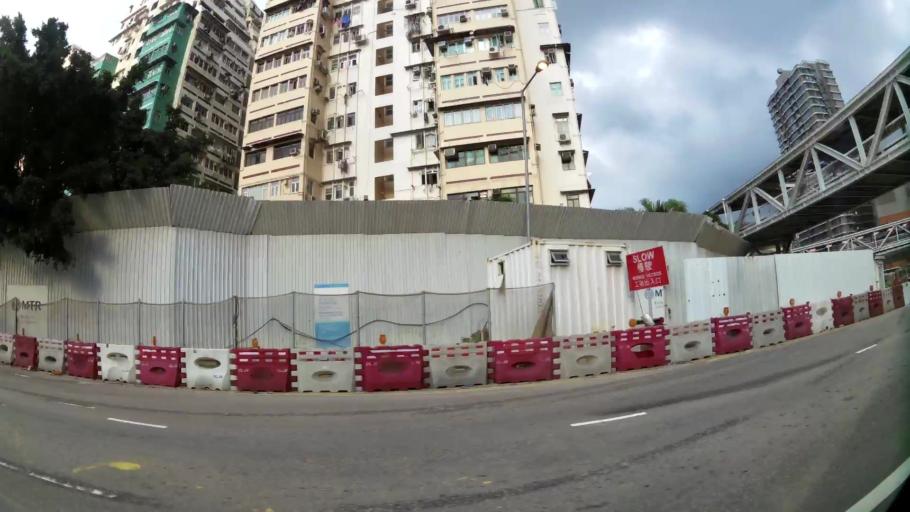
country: HK
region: Kowloon City
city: Kowloon
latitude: 22.3072
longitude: 114.1652
